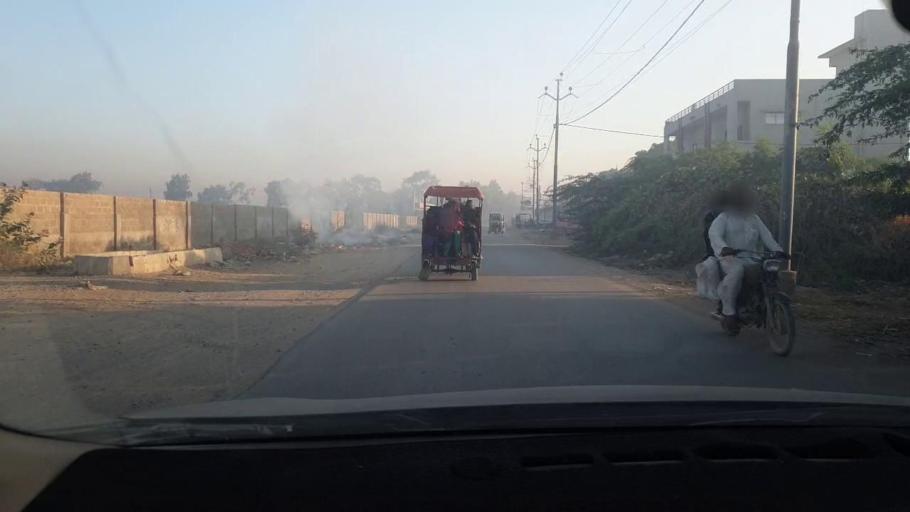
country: PK
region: Sindh
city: Malir Cantonment
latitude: 25.0045
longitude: 67.1528
